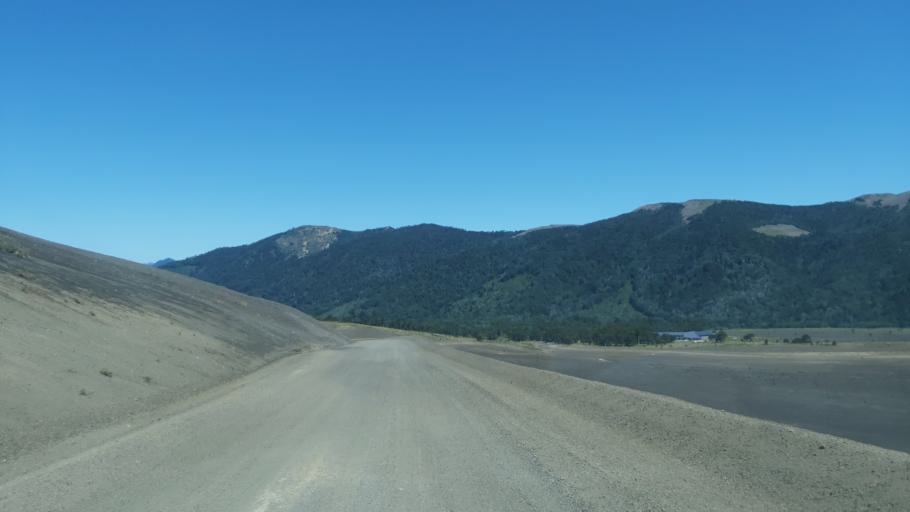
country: CL
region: Araucania
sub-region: Provincia de Cautin
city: Vilcun
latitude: -38.4100
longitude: -71.5424
